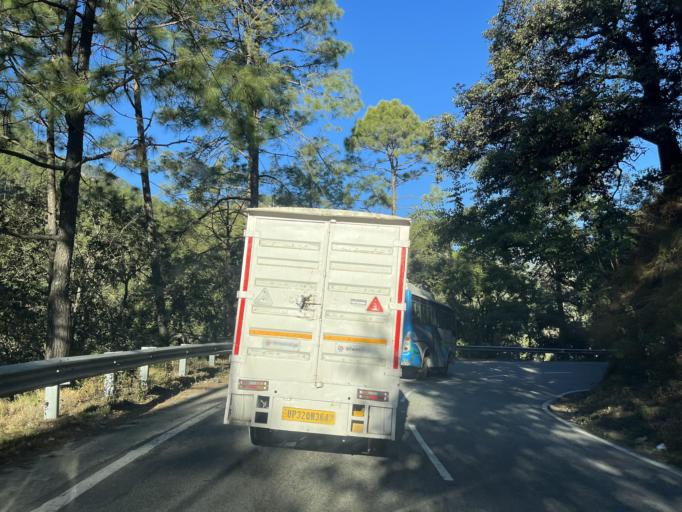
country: IN
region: Uttarakhand
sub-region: Naini Tal
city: Bhowali
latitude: 29.3993
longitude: 79.5085
